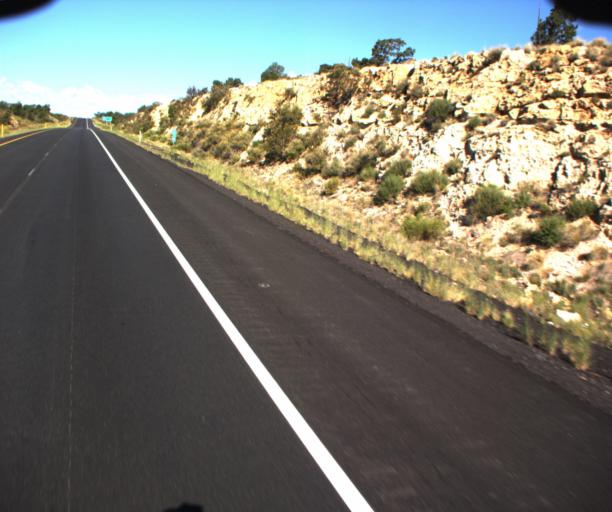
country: US
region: Arizona
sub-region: Coconino County
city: Flagstaff
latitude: 35.2017
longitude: -111.4268
